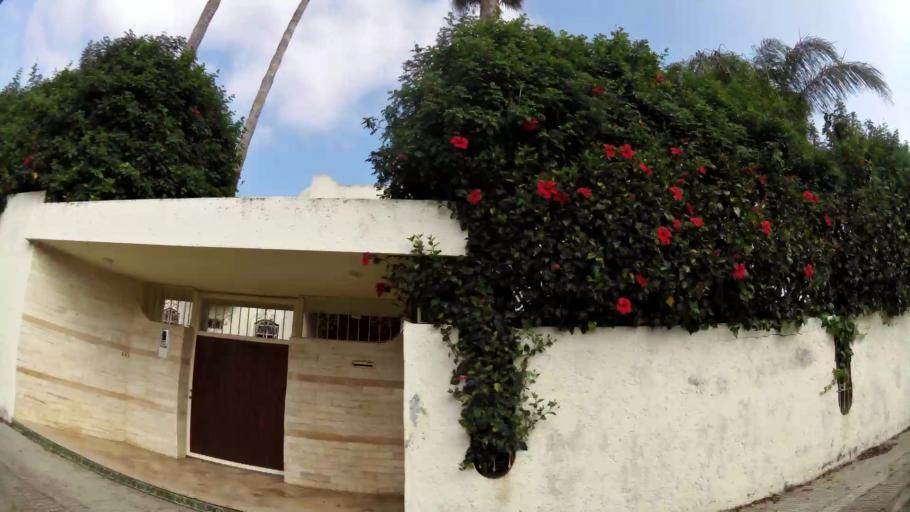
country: MA
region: Rabat-Sale-Zemmour-Zaer
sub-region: Rabat
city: Rabat
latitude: 33.9678
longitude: -6.8513
